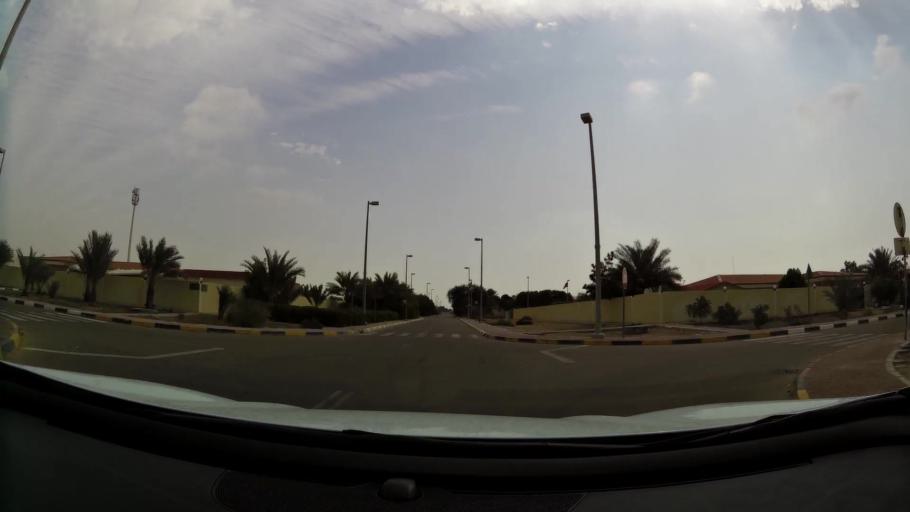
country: AE
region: Abu Dhabi
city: Abu Dhabi
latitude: 24.5217
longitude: 54.6791
